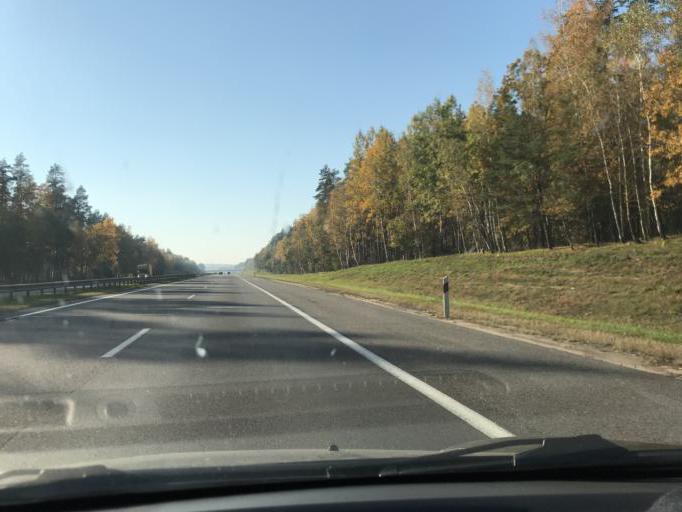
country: BY
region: Minsk
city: Pryvol'ny
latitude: 53.7969
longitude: 27.7563
